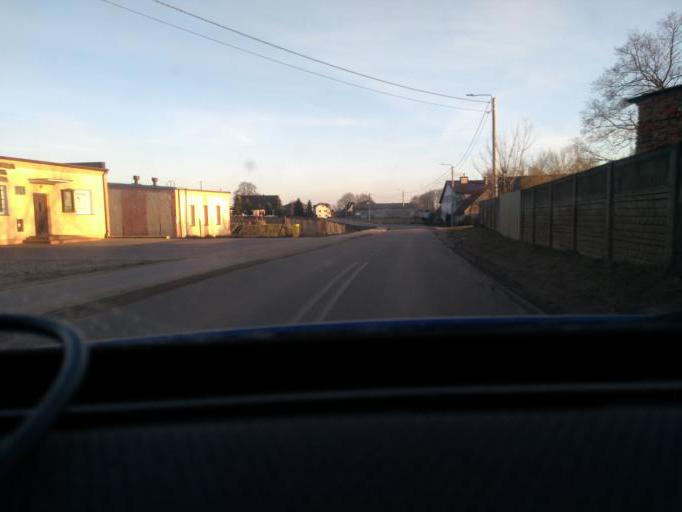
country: PL
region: Pomeranian Voivodeship
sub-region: Powiat kartuski
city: Przodkowo
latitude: 54.4132
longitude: 18.3204
